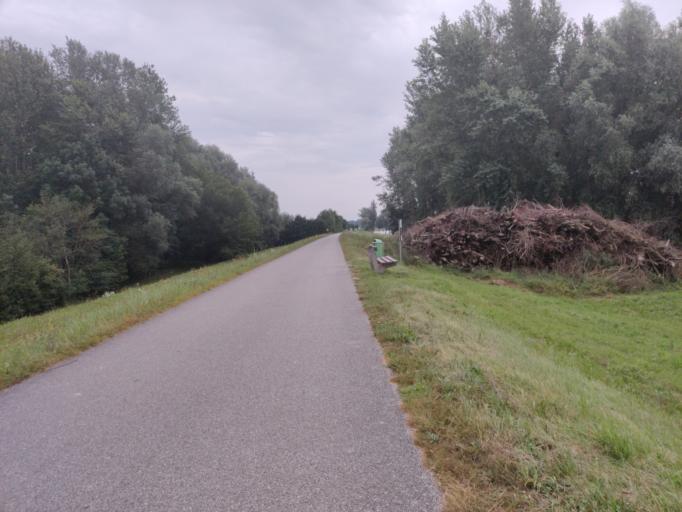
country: AT
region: Upper Austria
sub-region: Politischer Bezirk Perg
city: Perg
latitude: 48.2291
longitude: 14.5727
